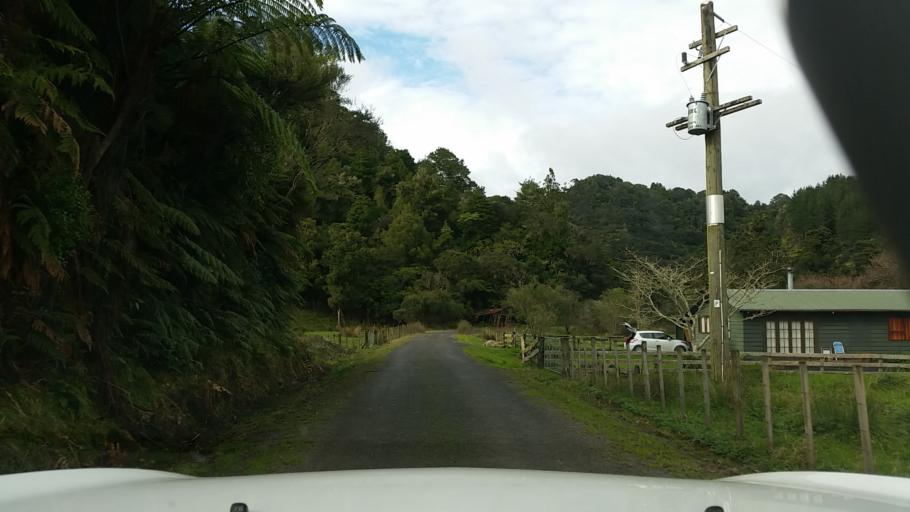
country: NZ
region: Taranaki
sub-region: New Plymouth District
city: Waitara
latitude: -38.8103
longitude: 174.6213
